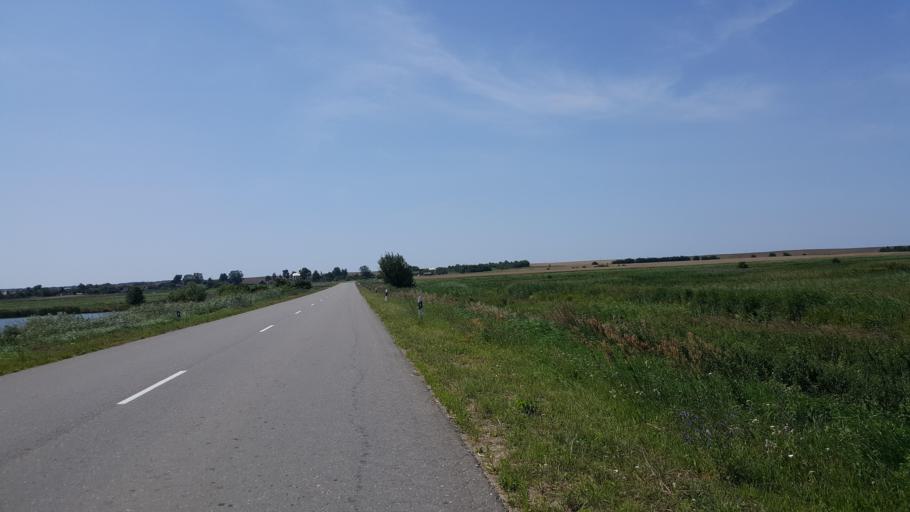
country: BY
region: Brest
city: Vysokaye
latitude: 52.3629
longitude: 23.5170
